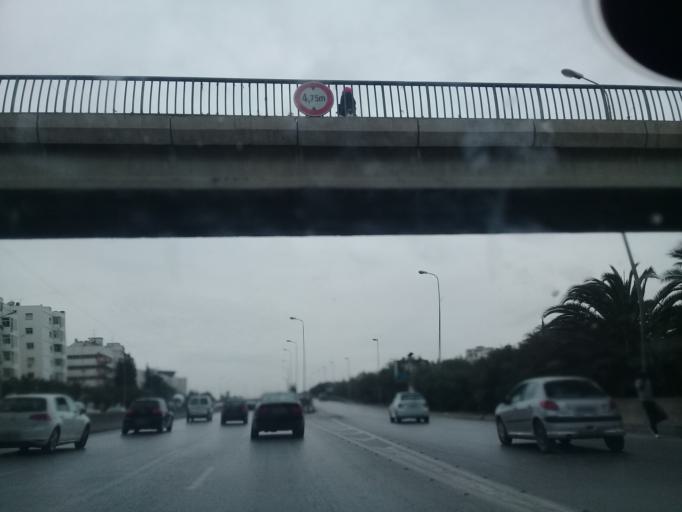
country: TN
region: Tunis
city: Tunis
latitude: 36.8359
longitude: 10.1608
